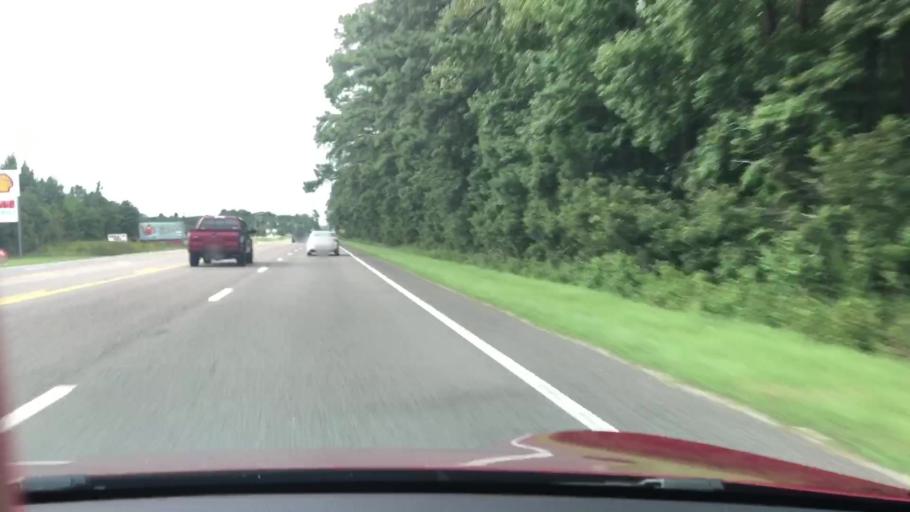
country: US
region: North Carolina
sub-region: Dare County
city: Southern Shores
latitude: 36.2233
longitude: -75.8705
